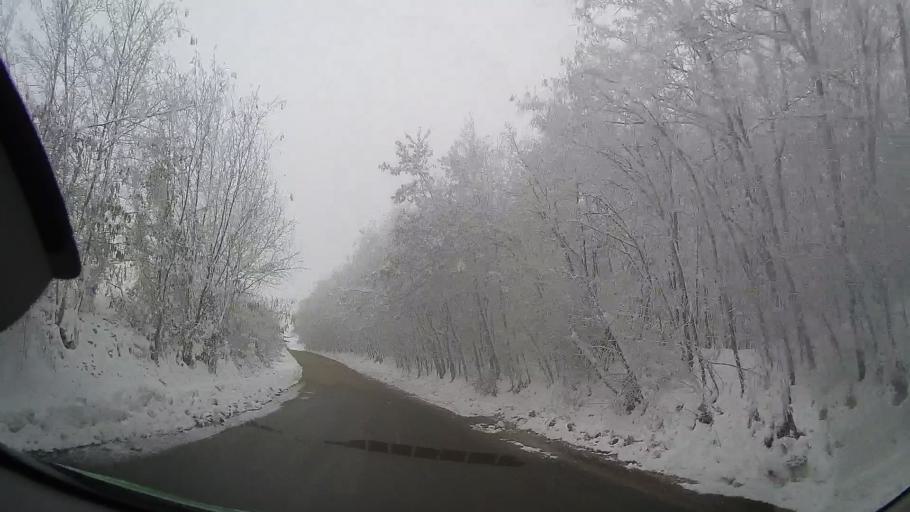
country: RO
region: Iasi
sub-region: Comuna Tansa
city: Suhulet
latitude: 46.8980
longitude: 27.2460
